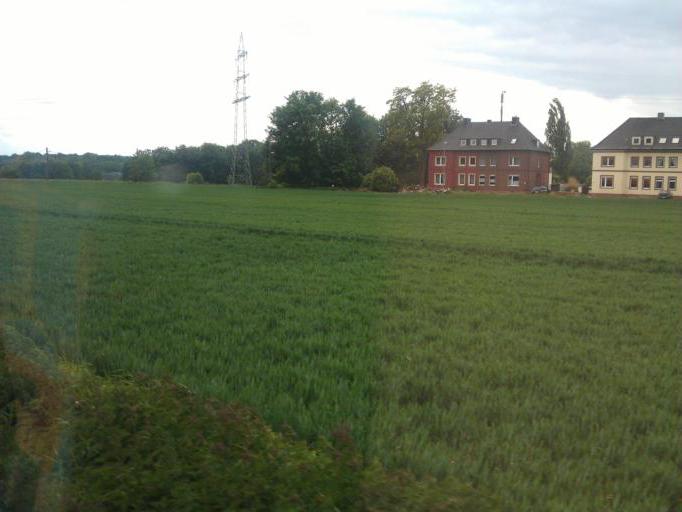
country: DE
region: North Rhine-Westphalia
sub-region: Regierungsbezirk Koln
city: Eschweiler
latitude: 50.8343
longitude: 6.3112
